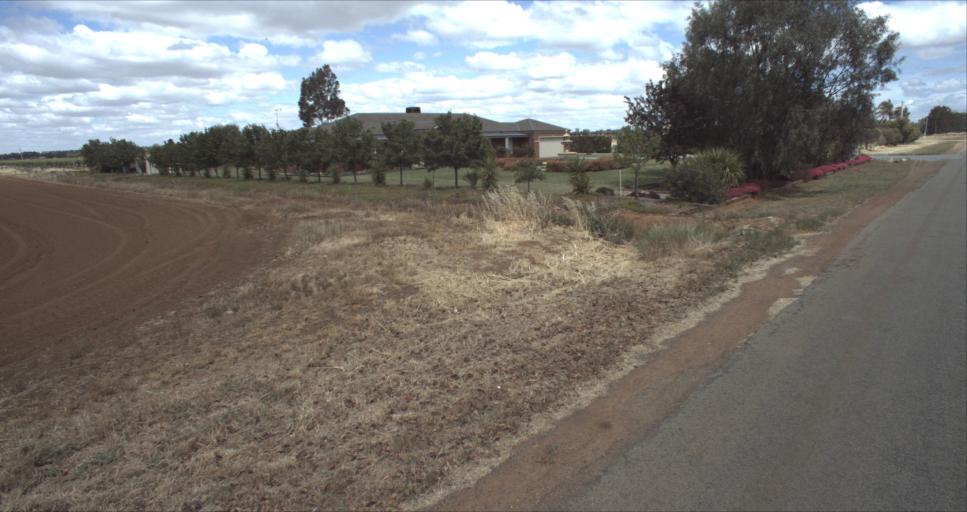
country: AU
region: New South Wales
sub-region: Leeton
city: Leeton
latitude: -34.5821
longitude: 146.3967
